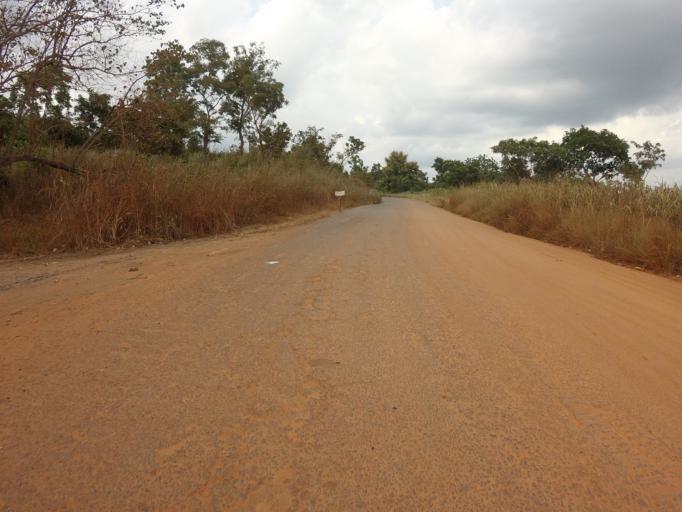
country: GH
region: Volta
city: Ho
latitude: 6.6744
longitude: 0.3513
